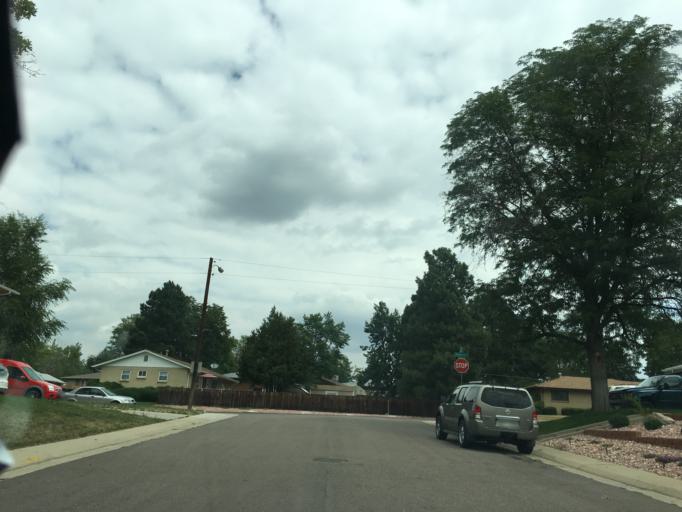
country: US
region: Colorado
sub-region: Arapahoe County
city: Sheridan
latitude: 39.6631
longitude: -105.0384
